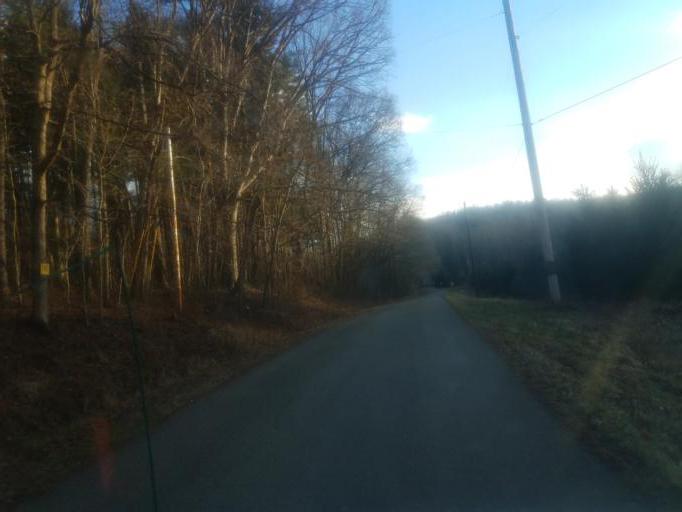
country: US
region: Ohio
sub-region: Sandusky County
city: Bellville
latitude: 40.5933
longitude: -82.3905
